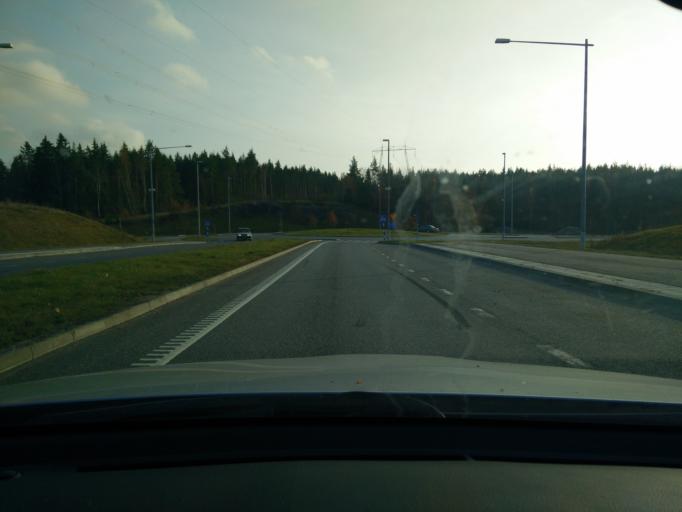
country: SE
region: Stockholm
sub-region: Sollentuna Kommun
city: Sollentuna
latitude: 59.4734
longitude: 17.9960
